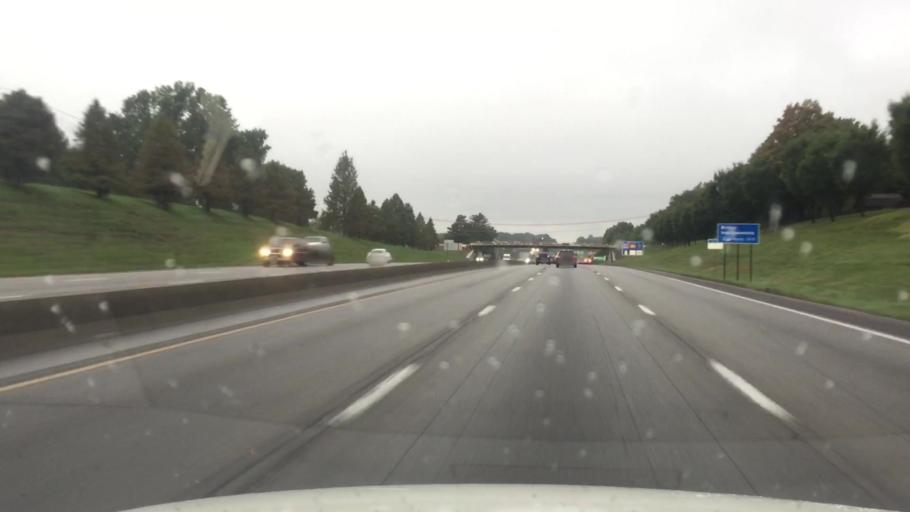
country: US
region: Missouri
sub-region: Jackson County
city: Independence
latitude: 39.0456
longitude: -94.4017
